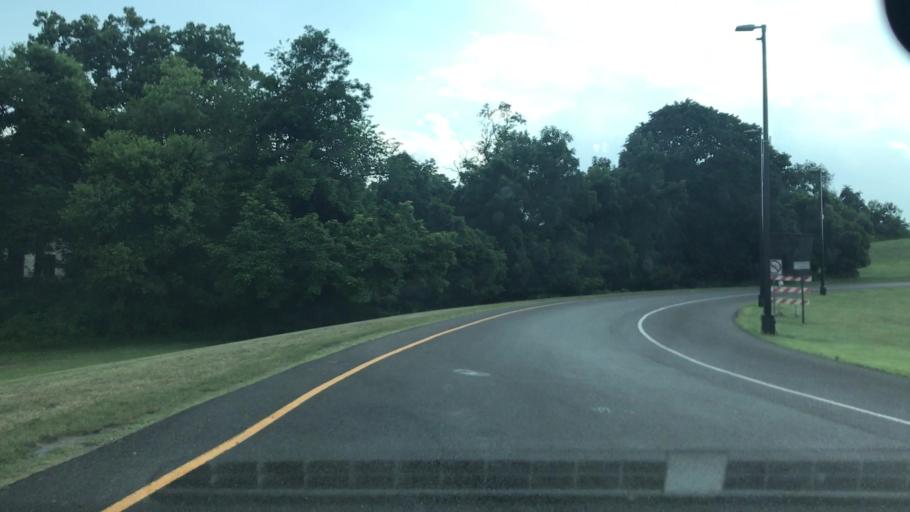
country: US
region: Pennsylvania
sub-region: Bucks County
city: New Hope
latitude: 40.3764
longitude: -74.9605
